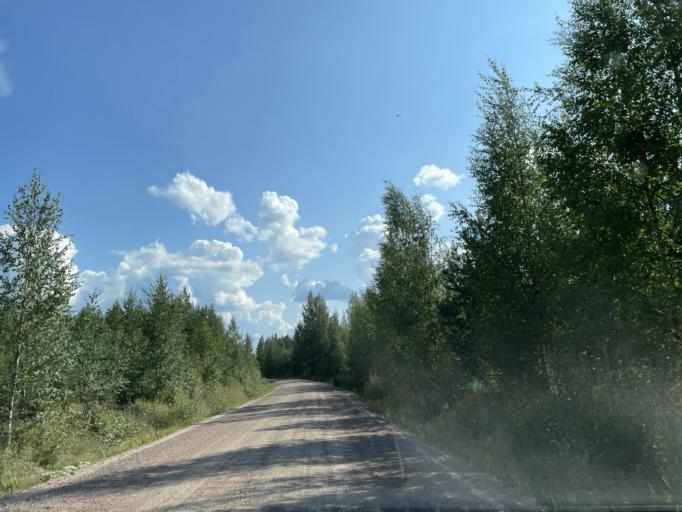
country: FI
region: Central Finland
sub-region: Saarijaervi-Viitasaari
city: Pihtipudas
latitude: 63.3486
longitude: 25.7900
